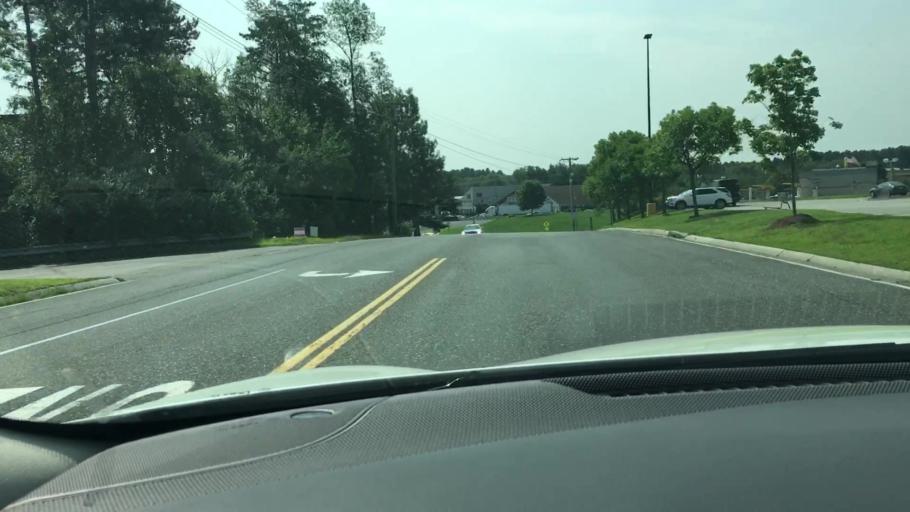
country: US
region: Massachusetts
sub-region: Worcester County
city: Northborough
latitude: 42.2848
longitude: -71.6548
